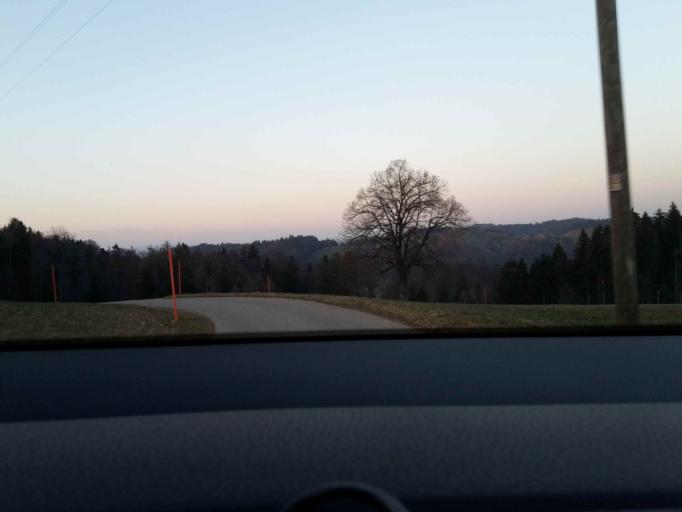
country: CH
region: Bern
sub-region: Oberaargau
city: Rohrbach
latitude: 47.1235
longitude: 7.7973
